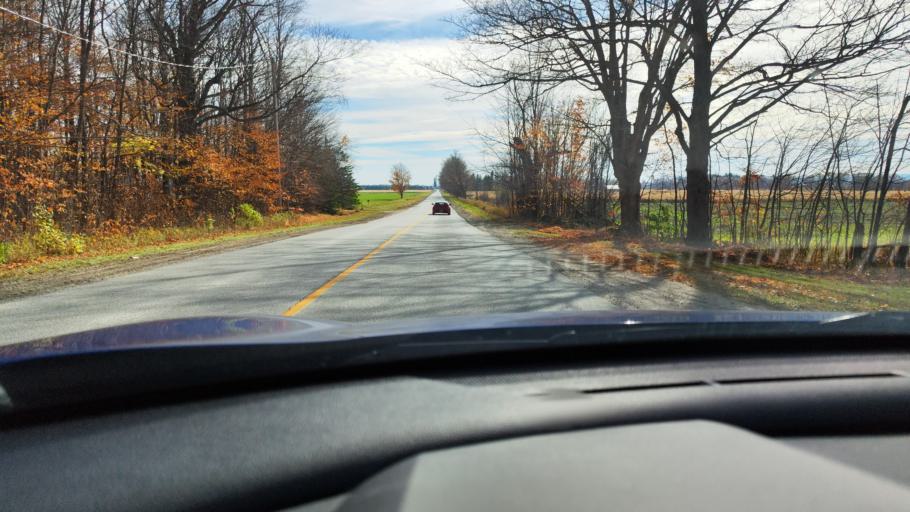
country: CA
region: Ontario
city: Wasaga Beach
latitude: 44.4550
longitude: -80.0021
